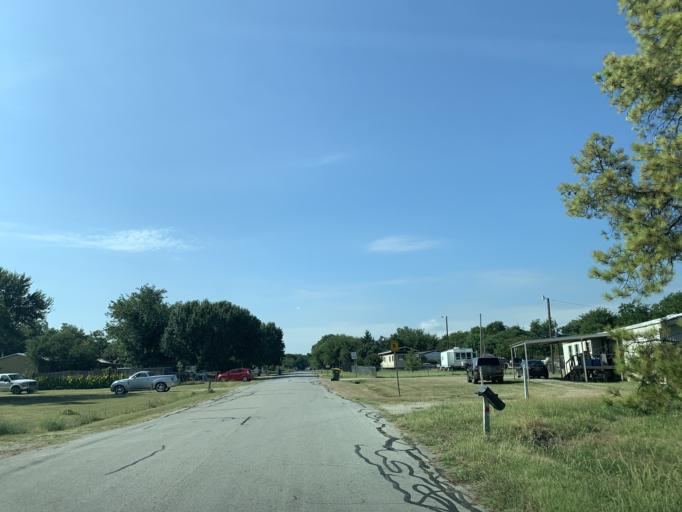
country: US
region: Texas
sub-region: Tarrant County
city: Lakeside
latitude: 32.8378
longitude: -97.4946
